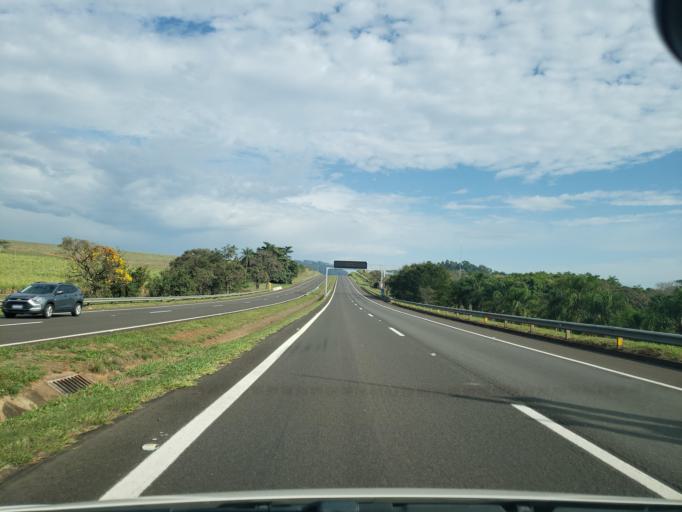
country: BR
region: Sao Paulo
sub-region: Dois Corregos
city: Dois Corregos
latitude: -22.2441
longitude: -48.3124
